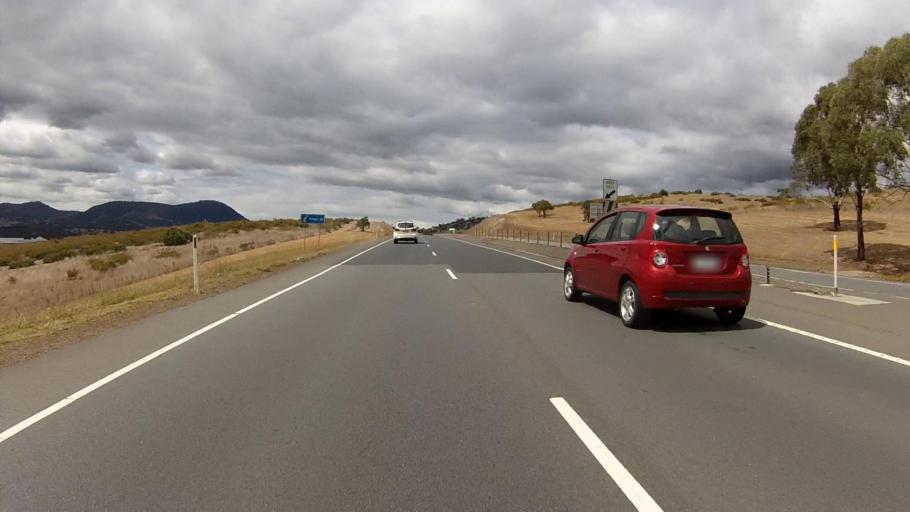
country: AU
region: Tasmania
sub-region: Glenorchy
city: Granton
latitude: -42.7590
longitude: 147.2313
